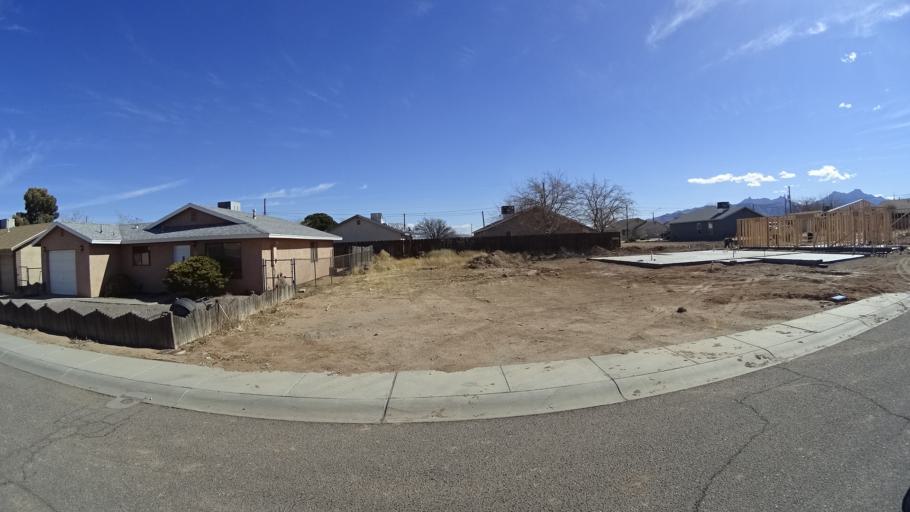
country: US
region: Arizona
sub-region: Mohave County
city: New Kingman-Butler
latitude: 35.2293
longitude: -114.0191
